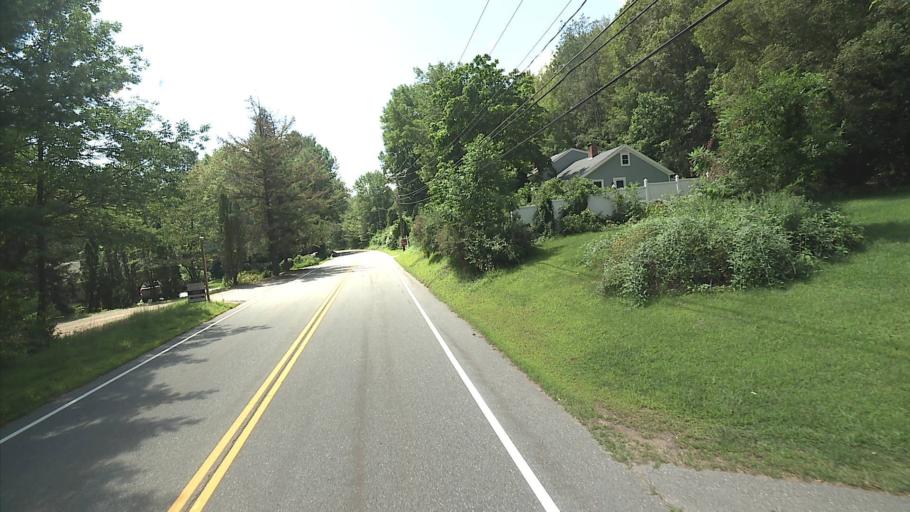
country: US
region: Connecticut
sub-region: Windham County
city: South Woodstock
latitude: 41.9508
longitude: -72.0759
